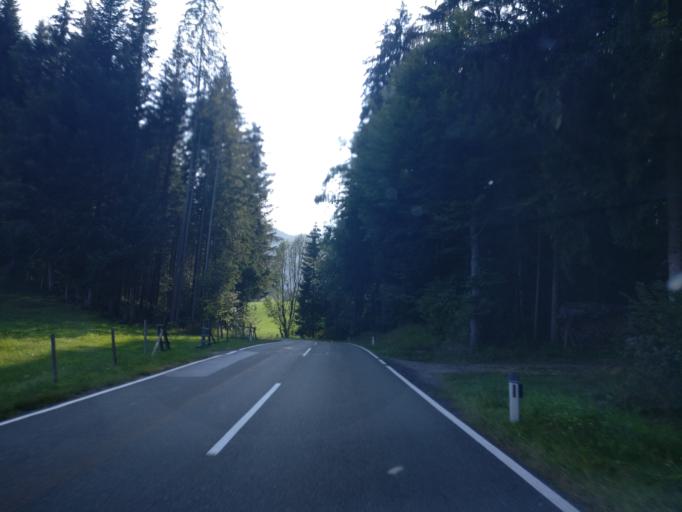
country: AT
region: Salzburg
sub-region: Politischer Bezirk Sankt Johann im Pongau
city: Werfenweng
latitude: 47.4550
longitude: 13.2348
